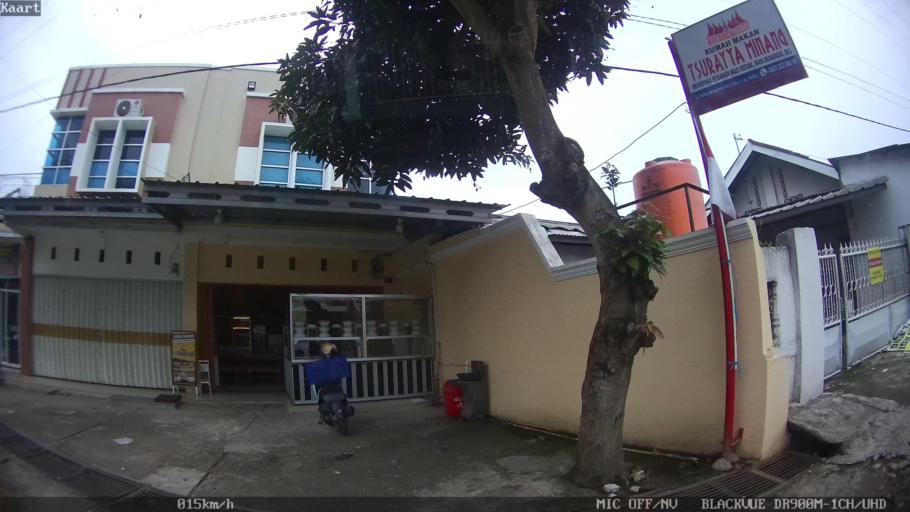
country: ID
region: Lampung
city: Kedaton
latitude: -5.3766
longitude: 105.2464
